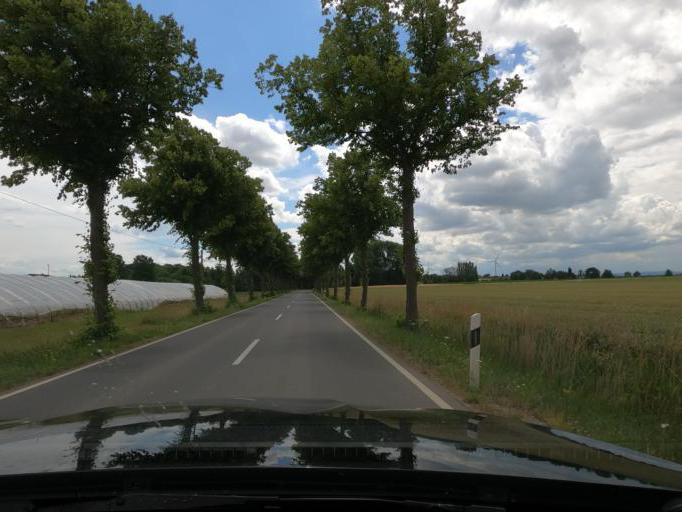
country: DE
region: Lower Saxony
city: Algermissen
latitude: 52.2768
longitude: 10.0136
